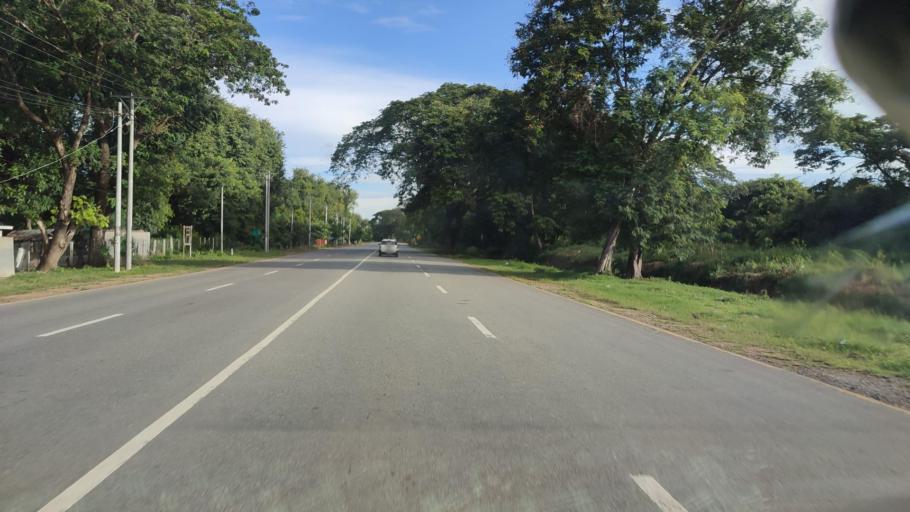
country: MM
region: Mandalay
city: Yamethin
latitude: 20.1901
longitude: 96.1851
